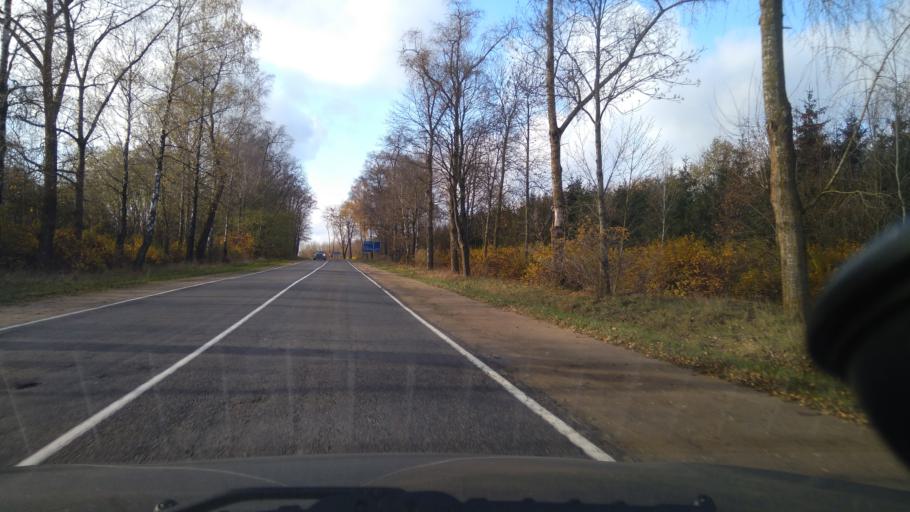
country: BY
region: Minsk
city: Slutsk
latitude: 53.2207
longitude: 27.5572
